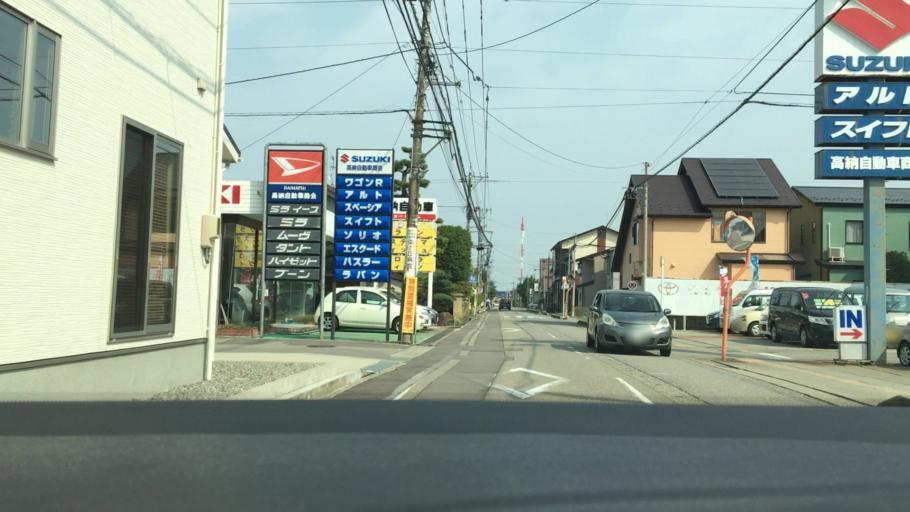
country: JP
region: Ishikawa
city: Nonoichi
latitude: 36.5250
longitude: 136.6045
